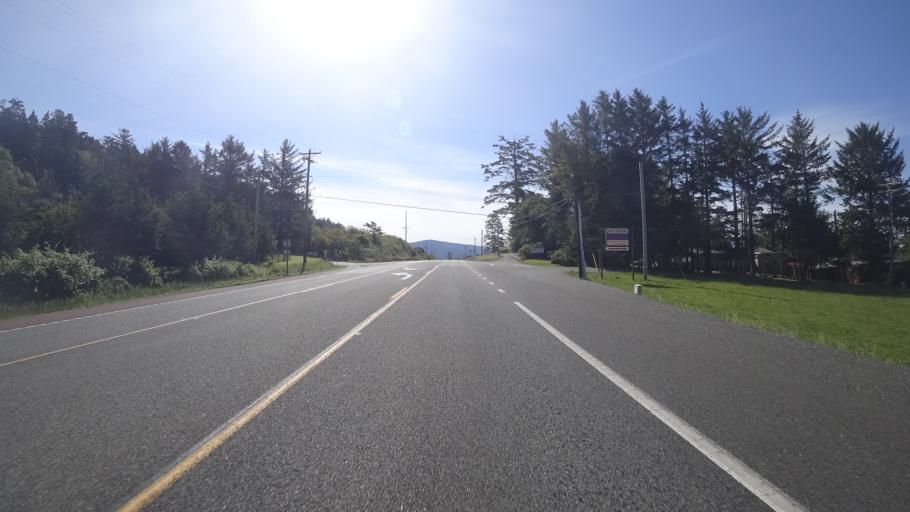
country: US
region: Oregon
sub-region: Curry County
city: Harbor
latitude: 41.9463
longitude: -124.1946
